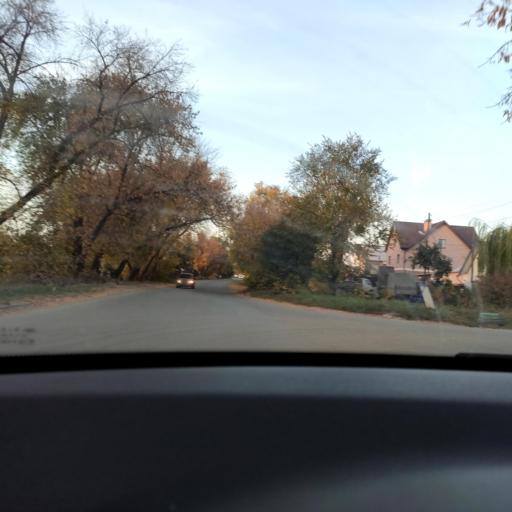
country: RU
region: Samara
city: Samara
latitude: 53.1882
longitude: 50.2123
